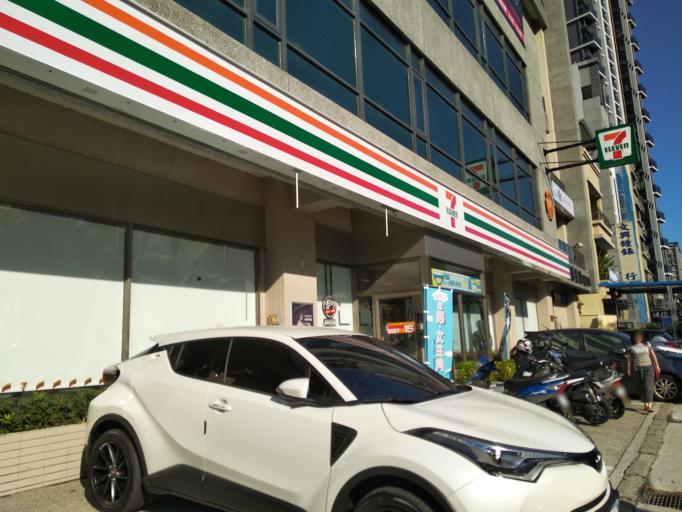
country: TW
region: Taiwan
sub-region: Hsinchu
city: Zhubei
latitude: 24.8248
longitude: 121.0293
